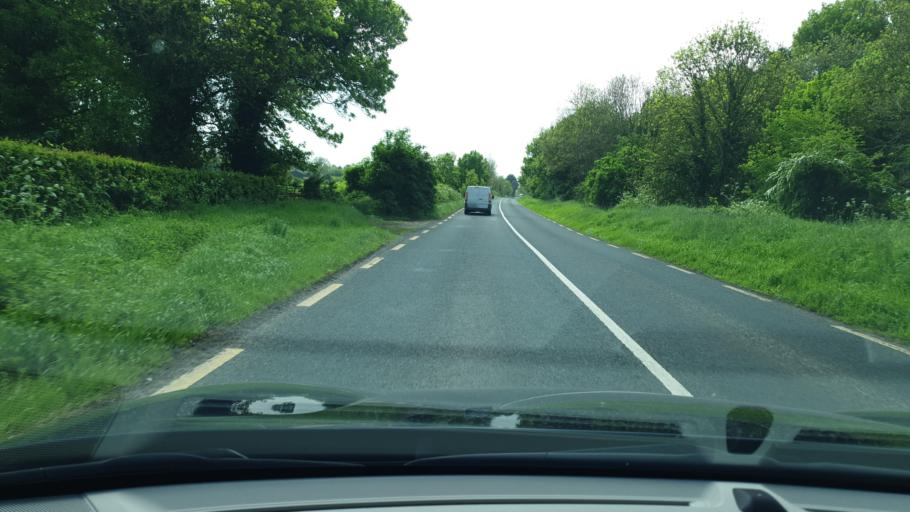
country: IE
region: Leinster
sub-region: An Mhi
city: Navan
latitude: 53.7531
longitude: -6.7209
